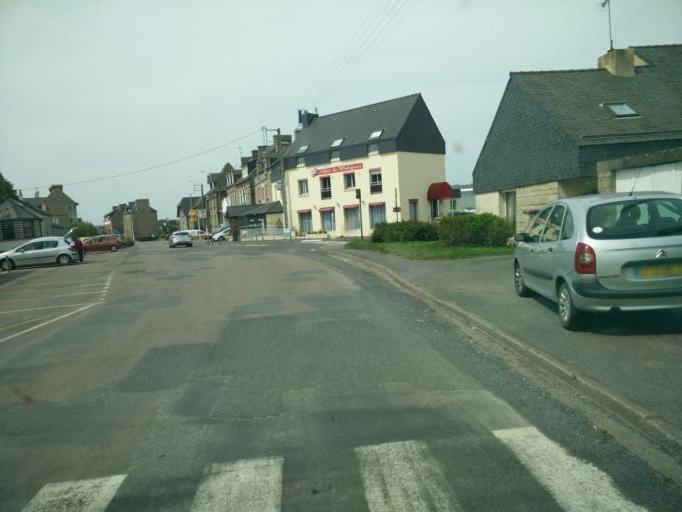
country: FR
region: Brittany
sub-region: Departement des Cotes-d'Armor
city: Matignon
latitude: 48.5949
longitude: -2.2866
